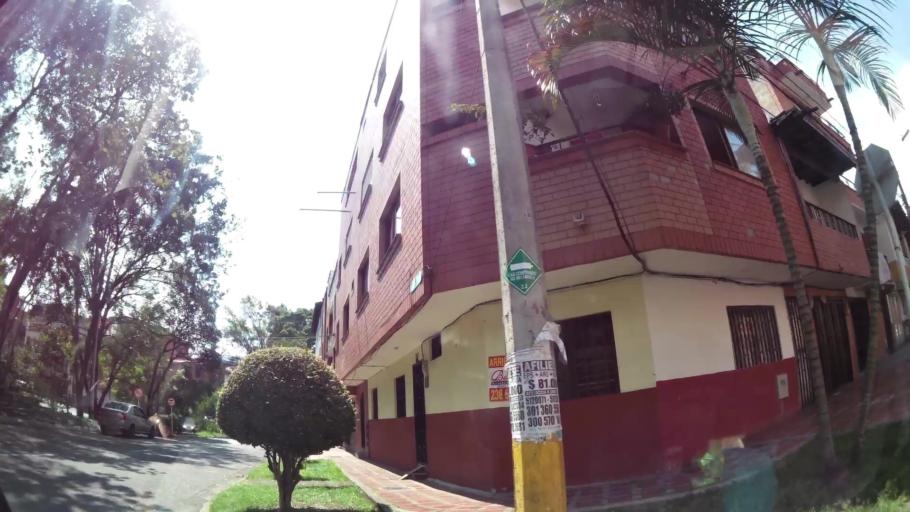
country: CO
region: Antioquia
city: Medellin
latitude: 6.2288
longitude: -75.5945
